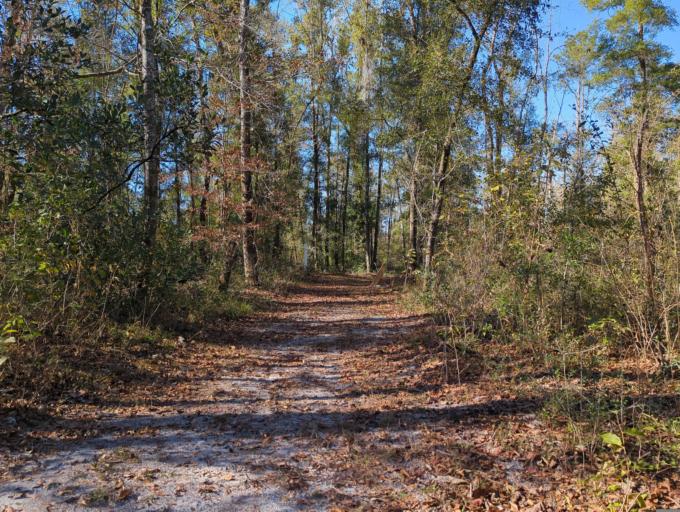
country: US
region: Florida
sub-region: Wakulla County
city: Crawfordville
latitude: 30.1854
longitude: -84.3263
